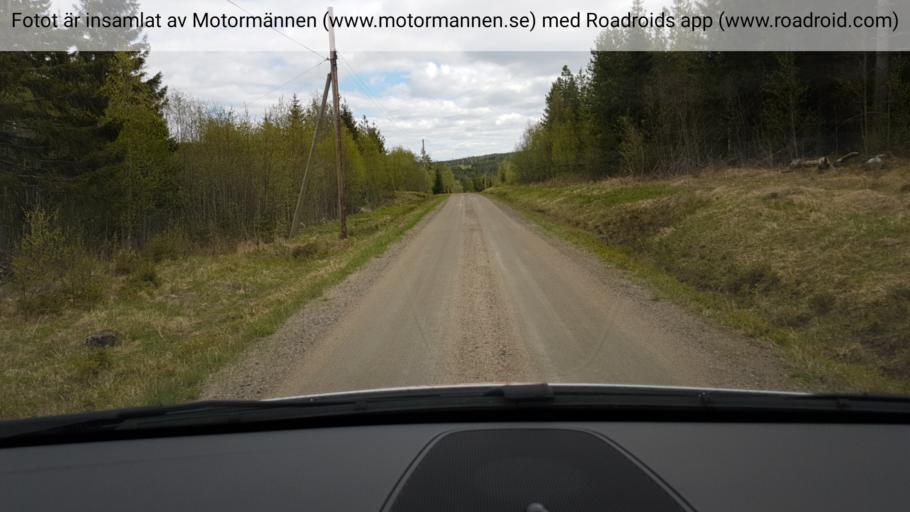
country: SE
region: Jaemtland
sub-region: Braecke Kommun
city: Braecke
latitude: 62.8079
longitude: 15.1070
